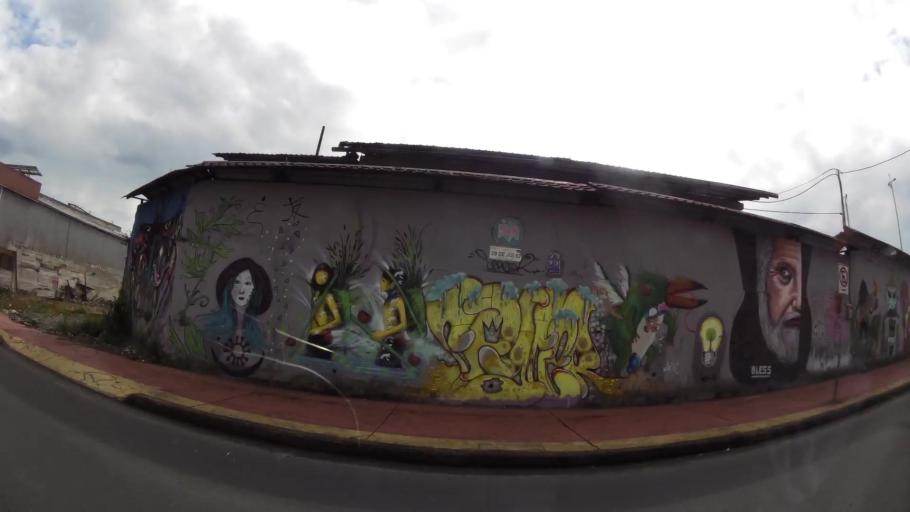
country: EC
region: Pastaza
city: Puyo
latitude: -1.4843
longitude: -77.9999
